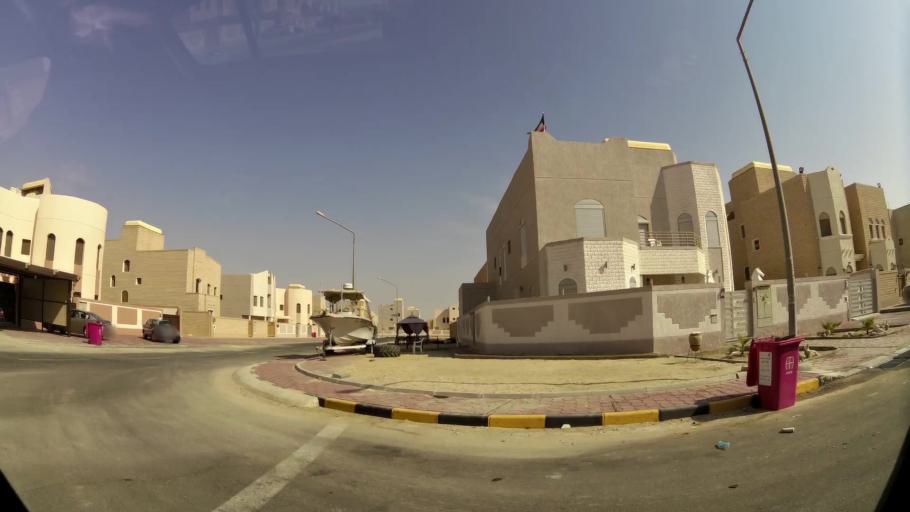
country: KW
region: Al Ahmadi
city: Al Wafrah
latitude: 28.7950
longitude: 48.0729
